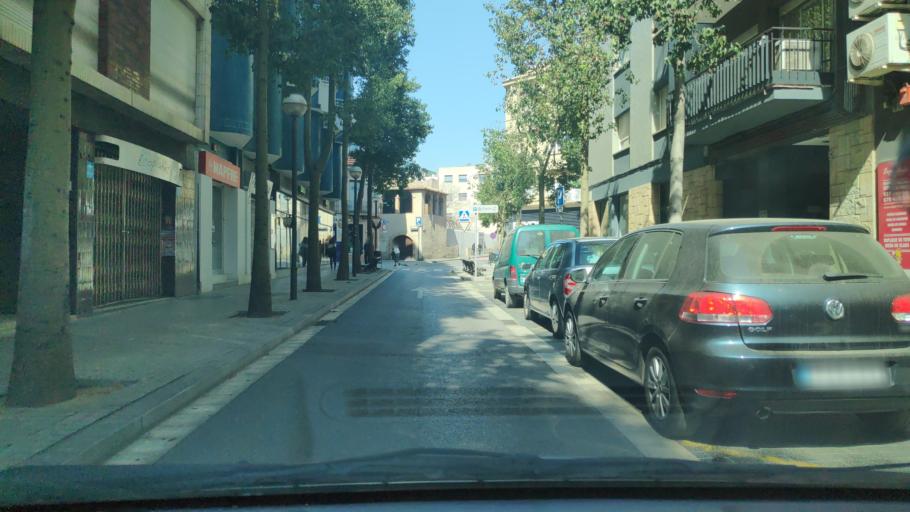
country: ES
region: Catalonia
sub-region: Provincia de Barcelona
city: Sabadell
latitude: 41.5464
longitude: 2.1102
